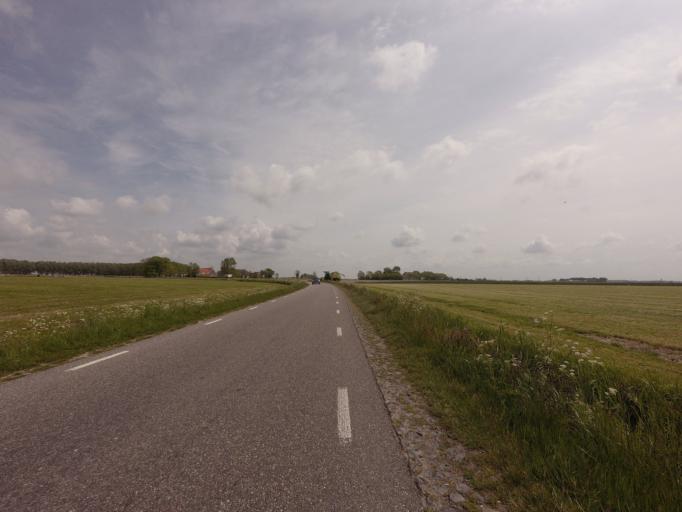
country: NL
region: Friesland
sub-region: Sudwest Fryslan
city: Bolsward
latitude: 53.1114
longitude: 5.4849
